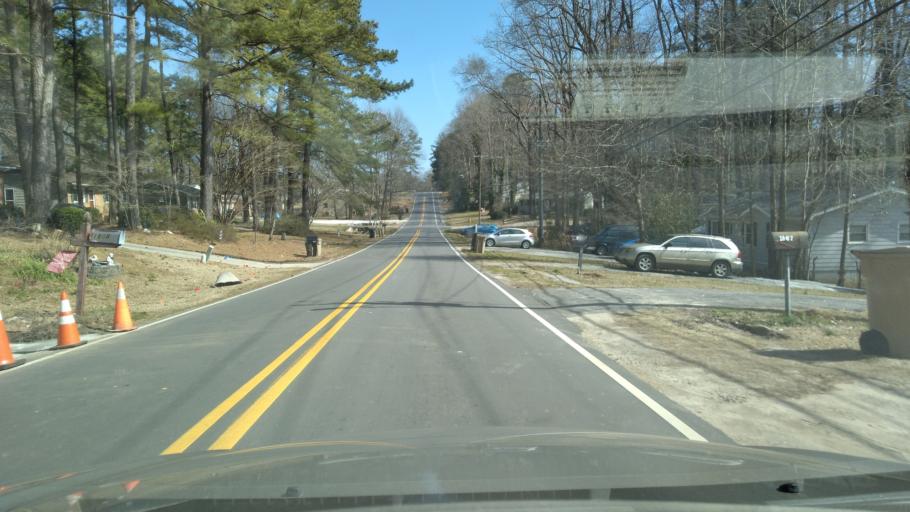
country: US
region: North Carolina
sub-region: Wake County
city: Garner
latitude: 35.7015
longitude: -78.6330
